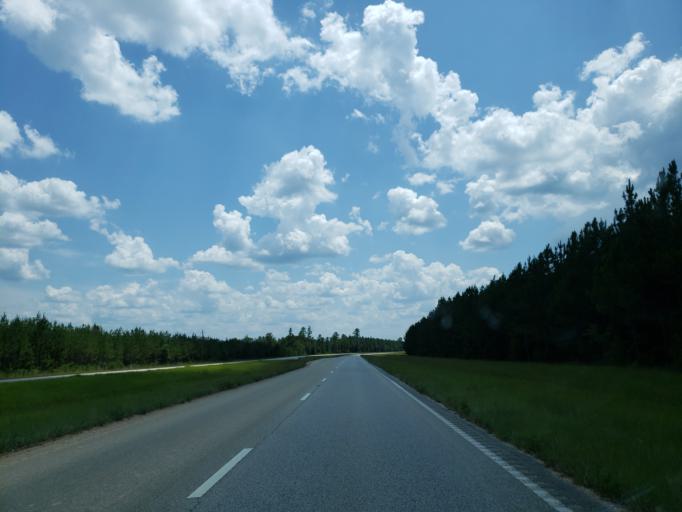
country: US
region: Mississippi
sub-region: Greene County
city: Leakesville
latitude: 31.2976
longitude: -88.5005
